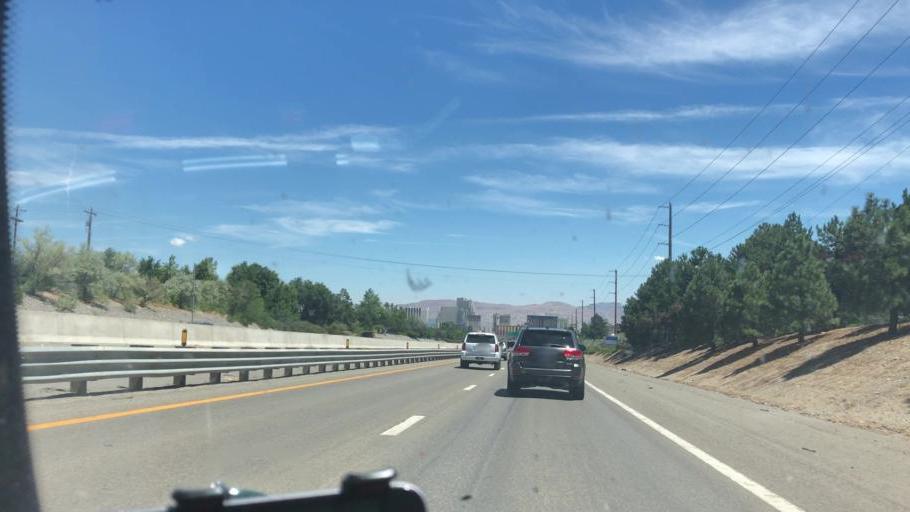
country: US
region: Nevada
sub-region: Washoe County
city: Reno
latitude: 39.5267
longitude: -119.8467
